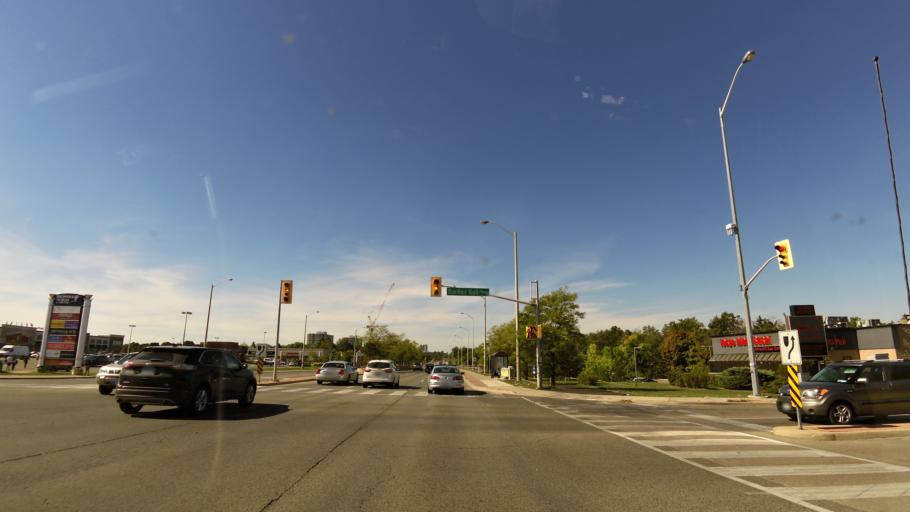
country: CA
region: Ontario
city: Brampton
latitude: 43.6676
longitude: -79.7351
